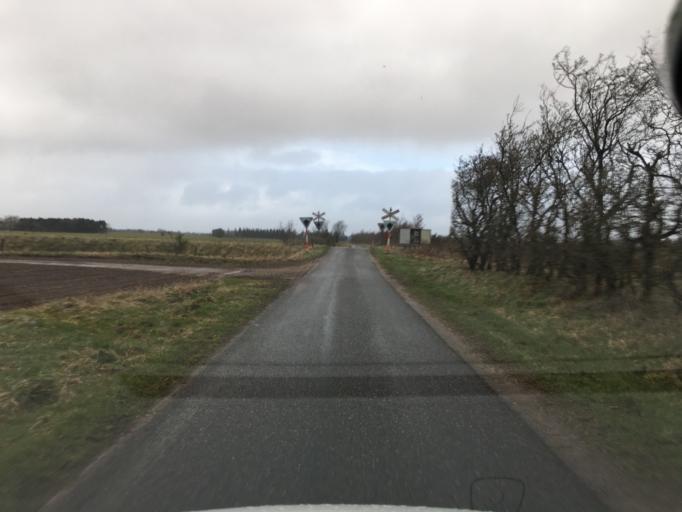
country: DK
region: South Denmark
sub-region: Aabenraa Kommune
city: Tinglev
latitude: 54.9471
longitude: 9.1609
